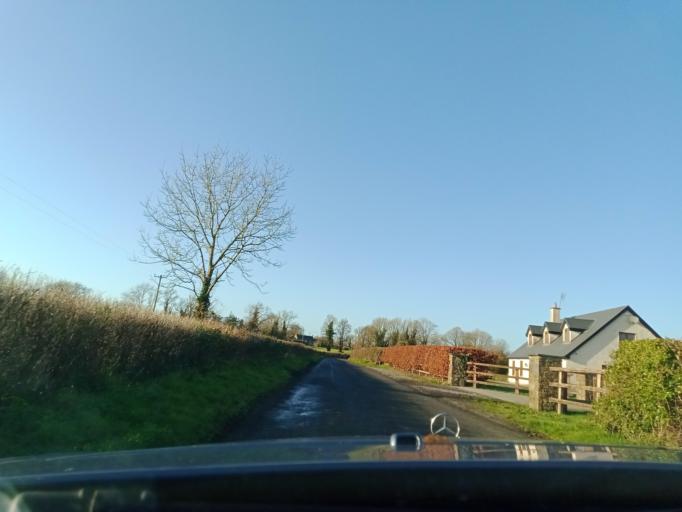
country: IE
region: Leinster
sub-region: Kilkenny
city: Callan
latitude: 52.5010
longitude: -7.3669
